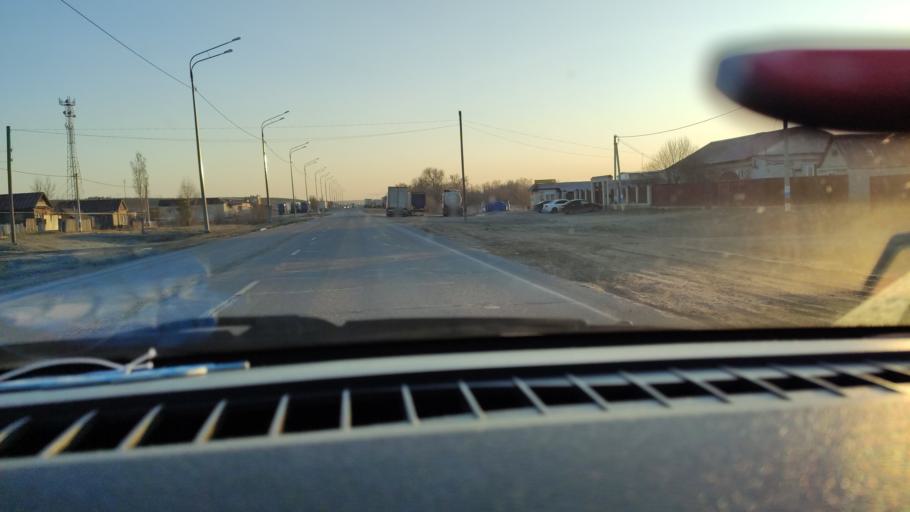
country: RU
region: Saratov
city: Sinodskoye
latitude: 51.9957
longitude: 46.6735
